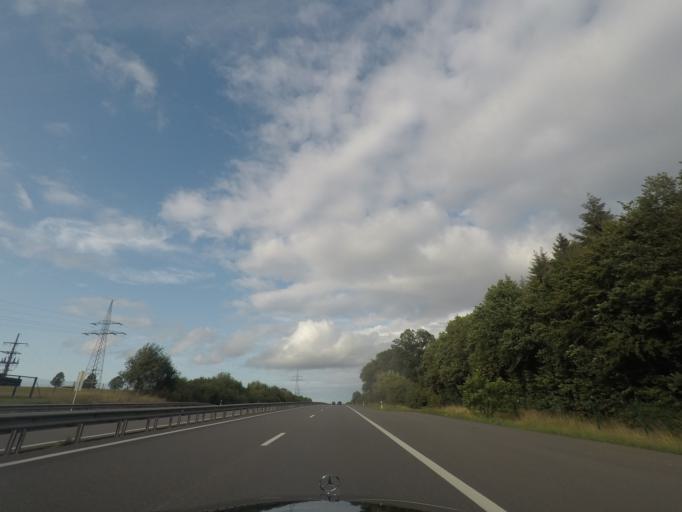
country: LU
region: Luxembourg
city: Colmar
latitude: 49.7854
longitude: 6.0977
